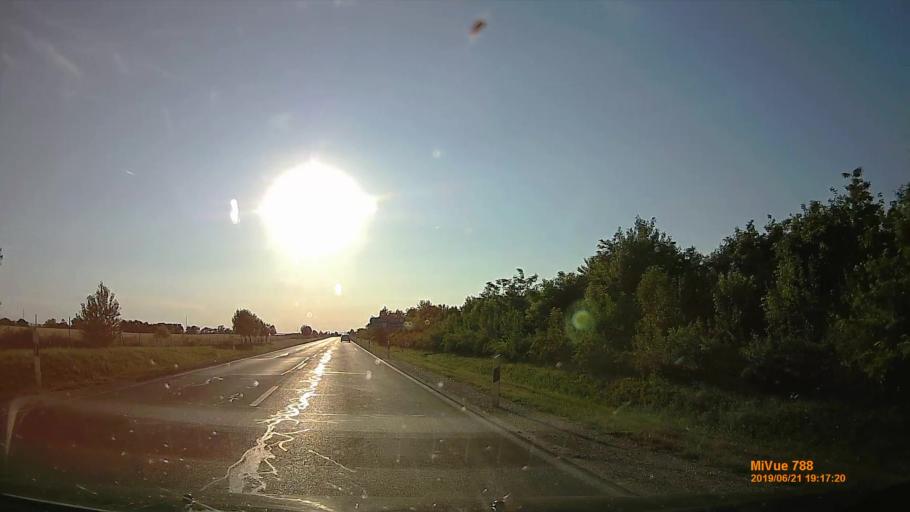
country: HU
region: Pest
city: Szazhalombatta
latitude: 47.3025
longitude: 18.8764
